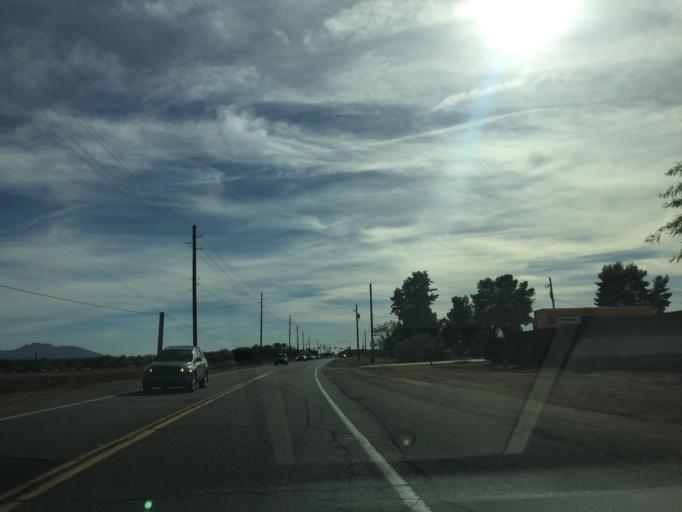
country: US
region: Arizona
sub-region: Maricopa County
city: Chandler
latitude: 33.2810
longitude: -111.7728
